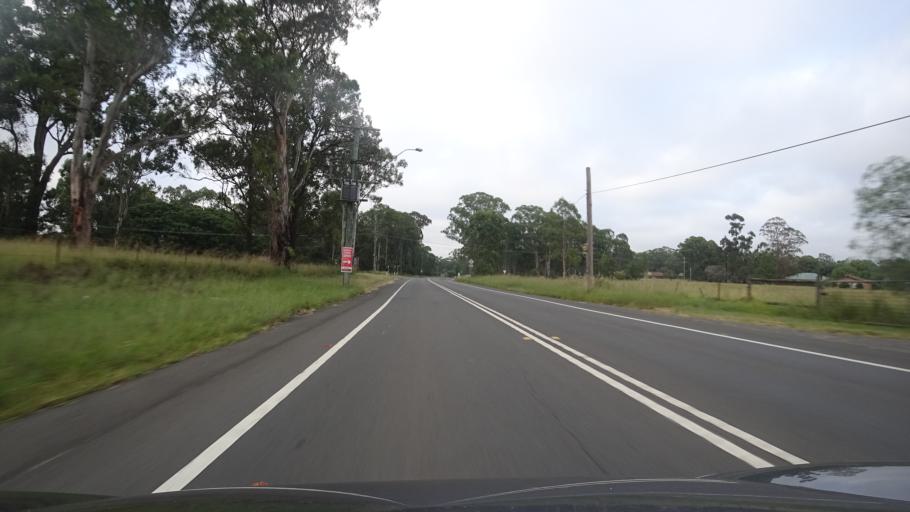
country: AU
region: New South Wales
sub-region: Blacktown
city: Rouse Hill
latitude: -33.6603
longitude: 150.9243
